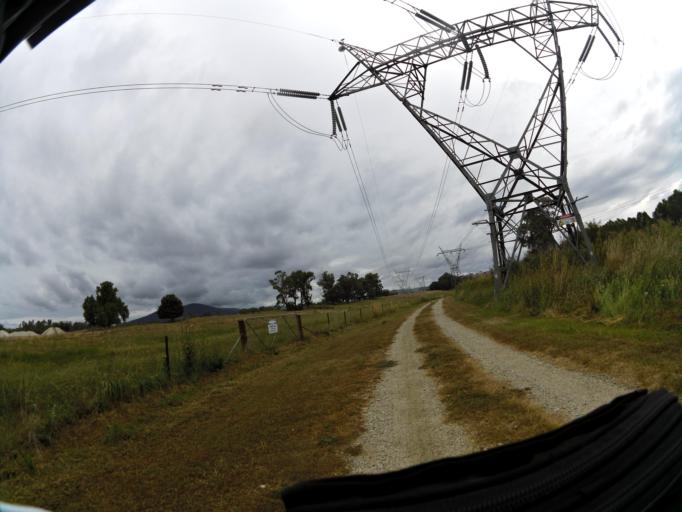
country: AU
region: New South Wales
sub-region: Albury Municipality
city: East Albury
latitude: -36.1507
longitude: 146.9579
